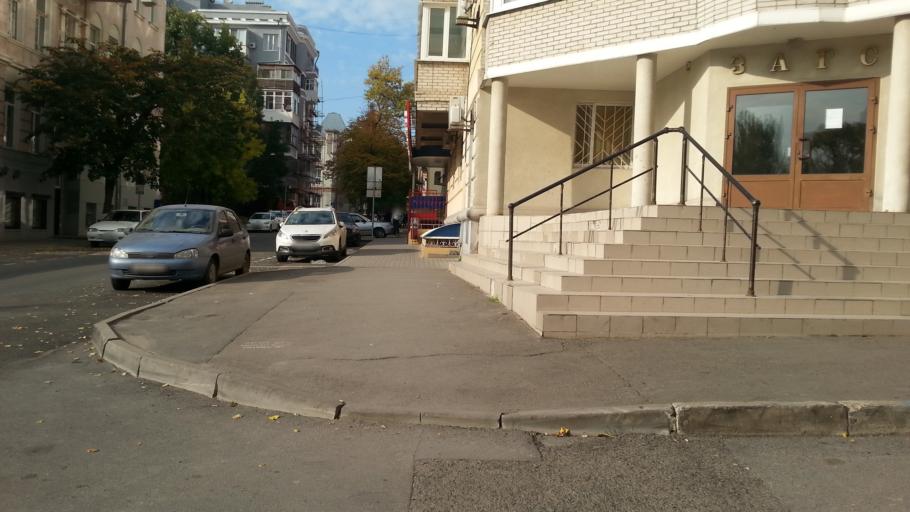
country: RU
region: Rostov
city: Rostov-na-Donu
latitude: 47.2243
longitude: 39.7090
